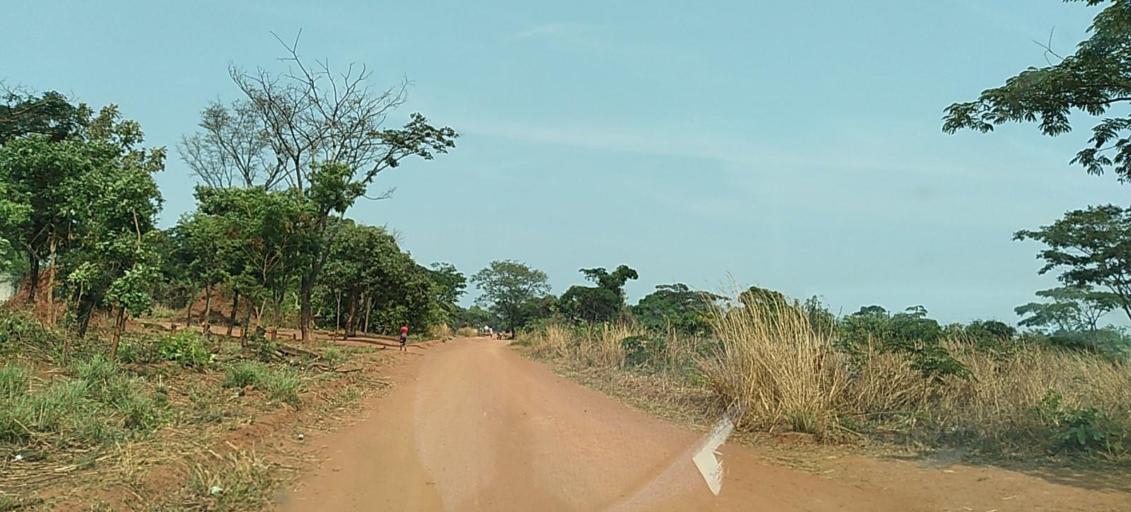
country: ZM
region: Copperbelt
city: Chililabombwe
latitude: -12.3407
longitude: 27.6885
